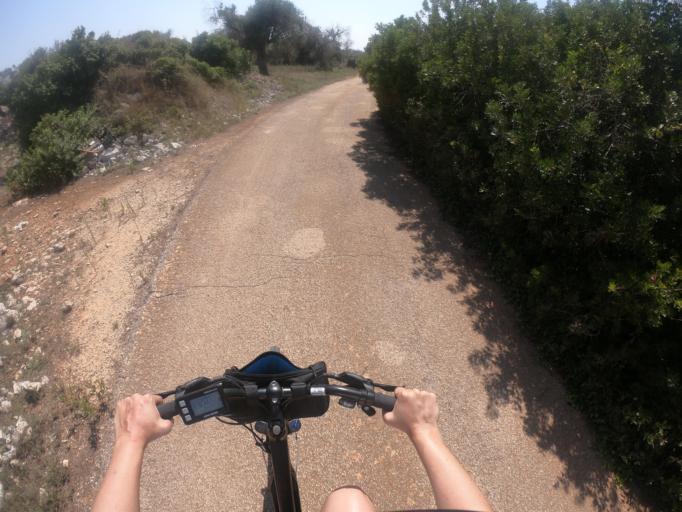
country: IT
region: Apulia
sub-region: Provincia di Lecce
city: Specchia
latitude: 39.9303
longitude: 18.2756
